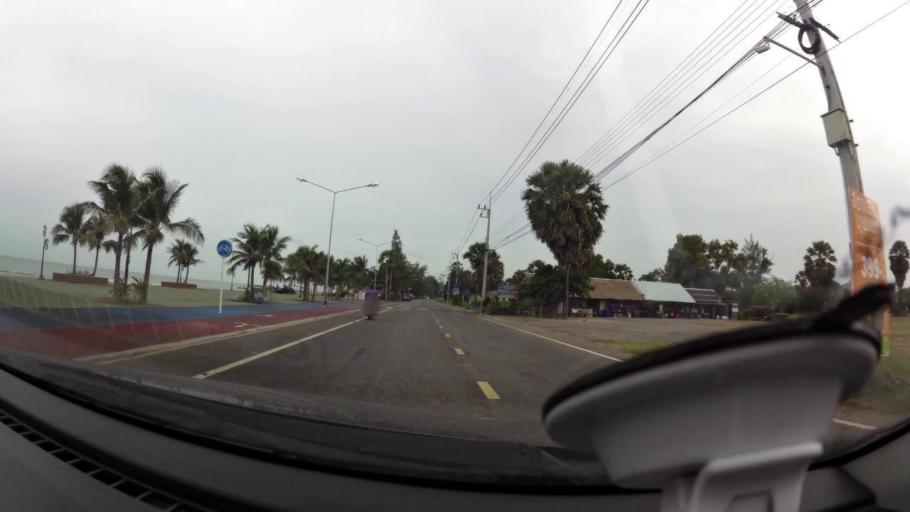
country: TH
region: Prachuap Khiri Khan
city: Pran Buri
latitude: 12.3714
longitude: 100.0000
